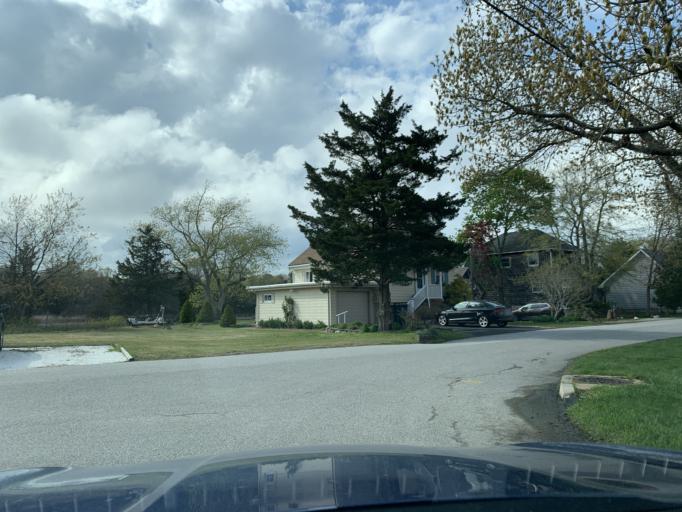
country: US
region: Rhode Island
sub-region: Washington County
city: North Kingstown
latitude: 41.5757
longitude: -71.4518
